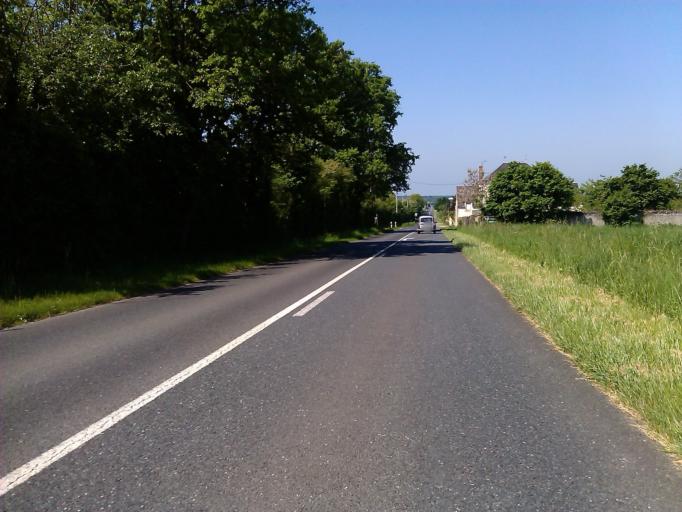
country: FR
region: Centre
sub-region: Departement de l'Indre
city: Le Pechereau
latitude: 46.5920
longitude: 1.5489
